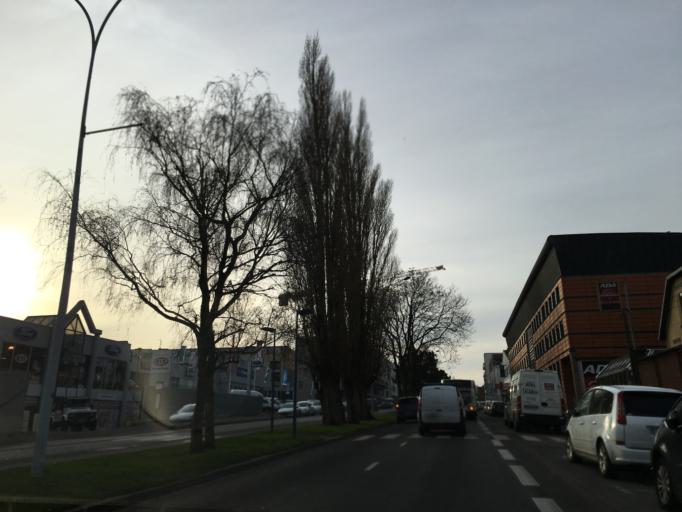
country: FR
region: Nord-Pas-de-Calais
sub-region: Departement du Pas-de-Calais
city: Arras
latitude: 50.2952
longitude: 2.7828
